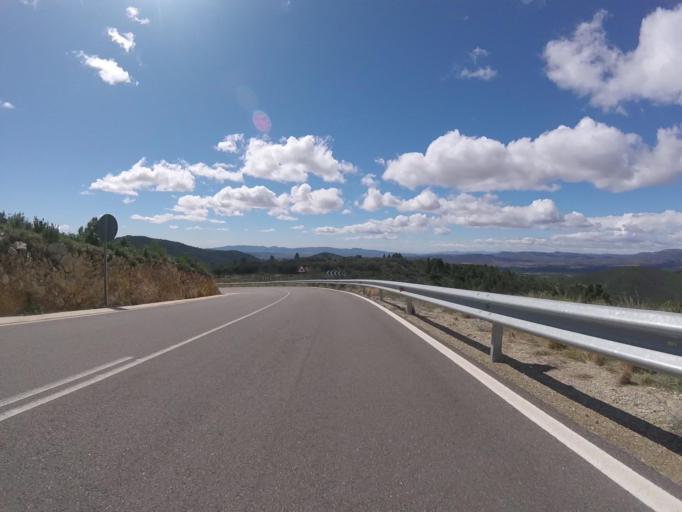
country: ES
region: Valencia
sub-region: Provincia de Castello
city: Culla
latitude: 40.2991
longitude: -0.1226
